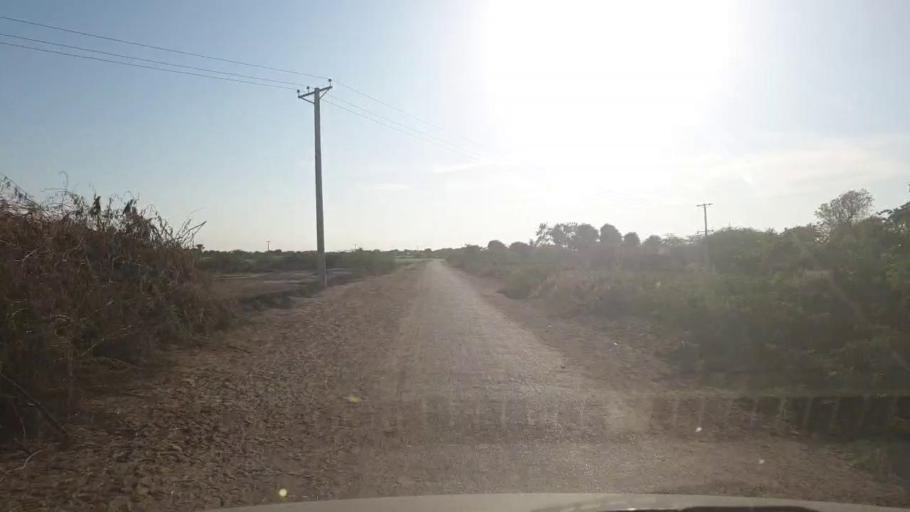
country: PK
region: Sindh
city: Dhoro Naro
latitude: 25.4180
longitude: 69.5588
